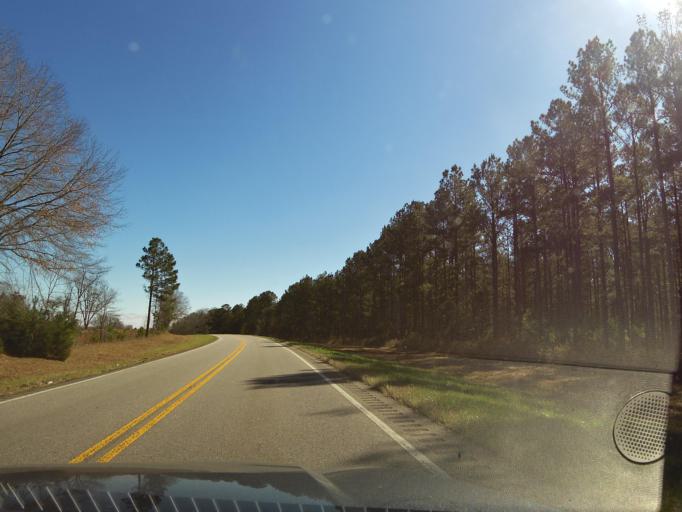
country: US
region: Alabama
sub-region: Bullock County
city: Union Springs
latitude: 32.1109
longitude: -85.5840
